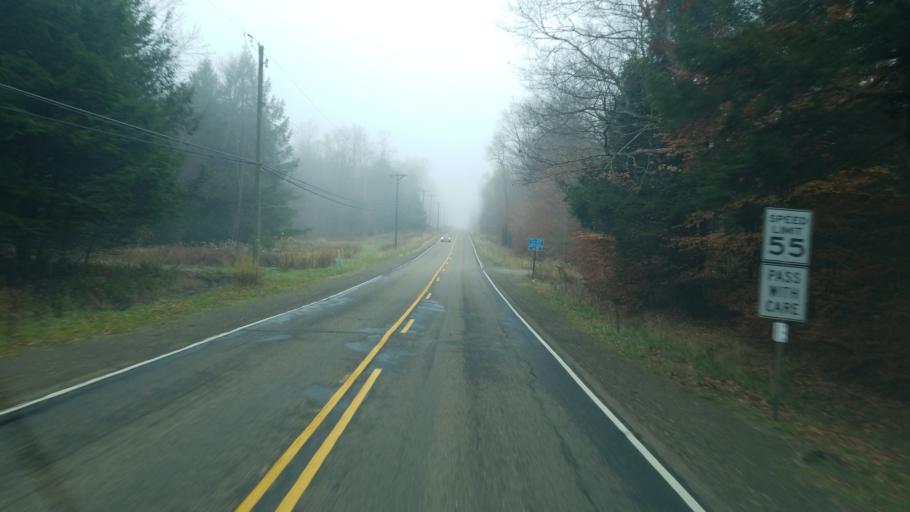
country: US
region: Pennsylvania
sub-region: McKean County
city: Smethport
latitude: 41.8132
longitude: -78.5490
